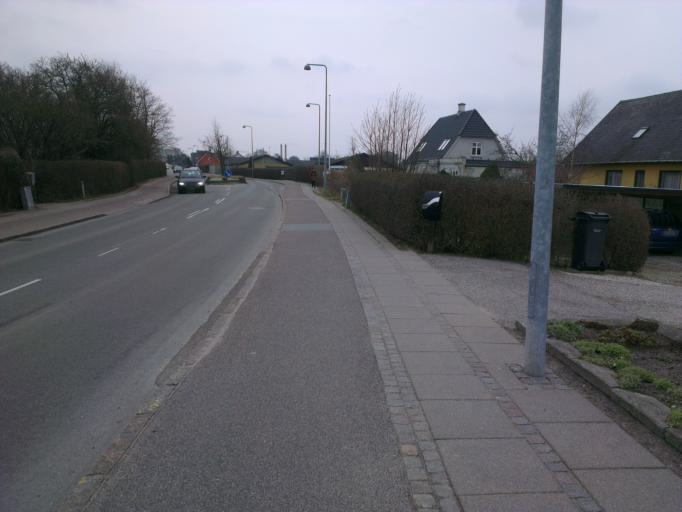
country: DK
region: Capital Region
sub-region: Frederikssund Kommune
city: Frederikssund
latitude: 55.8539
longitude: 12.0632
